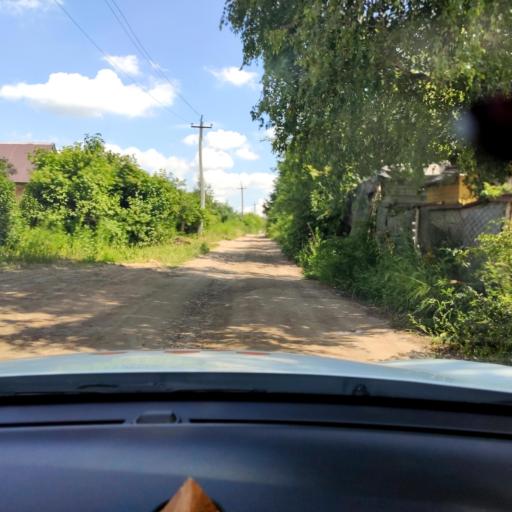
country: RU
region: Tatarstan
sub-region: Gorod Kazan'
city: Kazan
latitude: 55.8344
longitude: 49.2232
